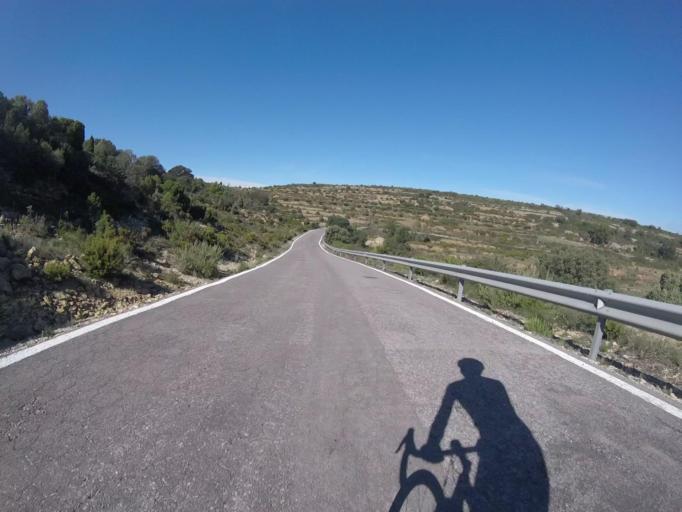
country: ES
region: Valencia
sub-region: Provincia de Castello
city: Sarratella
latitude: 40.3244
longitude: 0.0276
